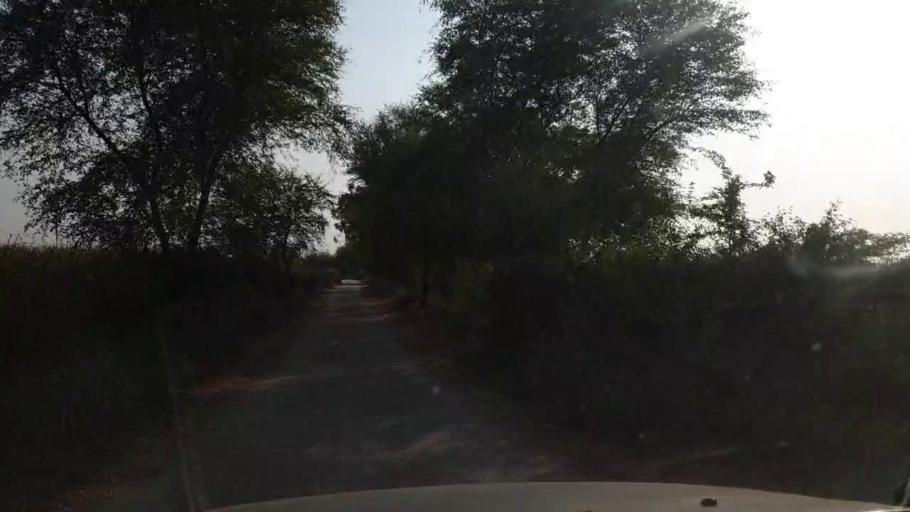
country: PK
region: Sindh
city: Bulri
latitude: 24.9457
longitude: 68.3423
